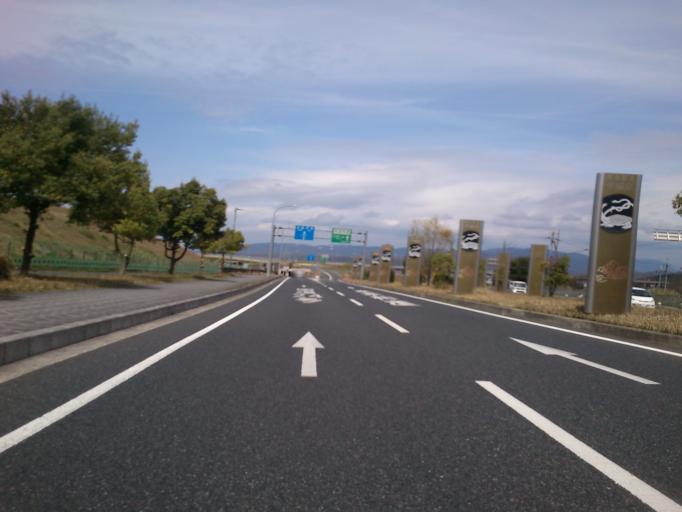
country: JP
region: Nara
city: Nara-shi
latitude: 34.7159
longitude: 135.8117
